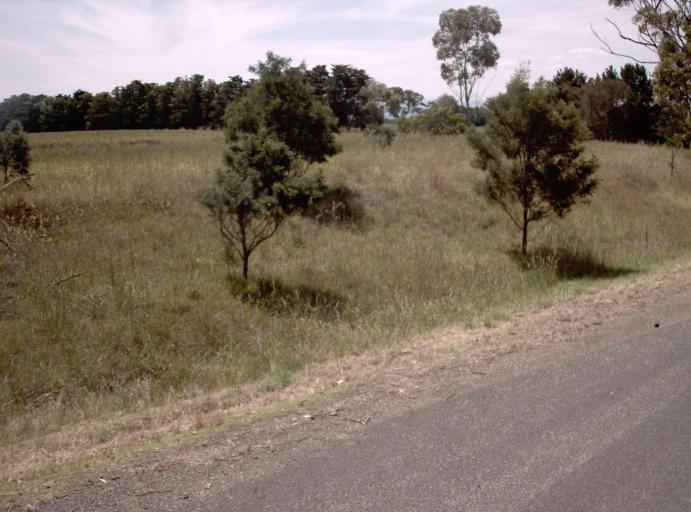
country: AU
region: Victoria
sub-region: Wellington
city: Sale
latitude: -37.9972
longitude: 147.0646
